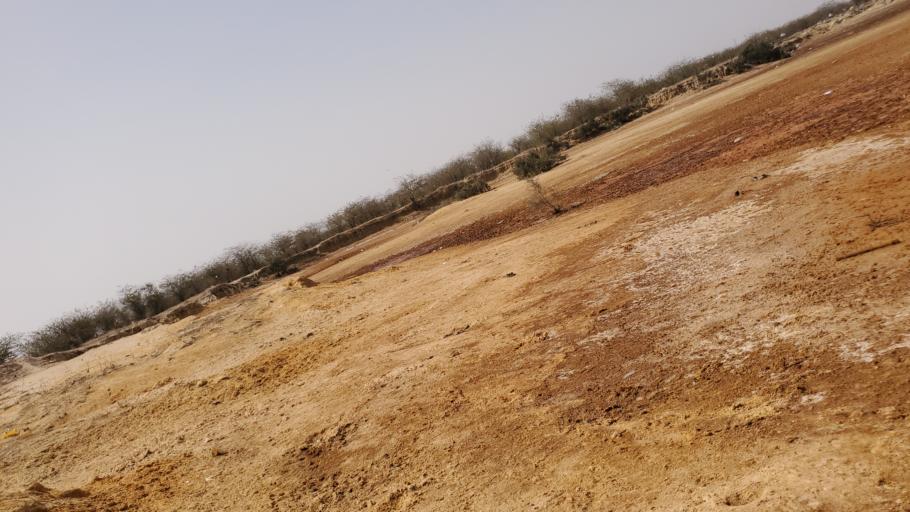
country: SN
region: Saint-Louis
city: Saint-Louis
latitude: 15.9494
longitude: -16.4299
